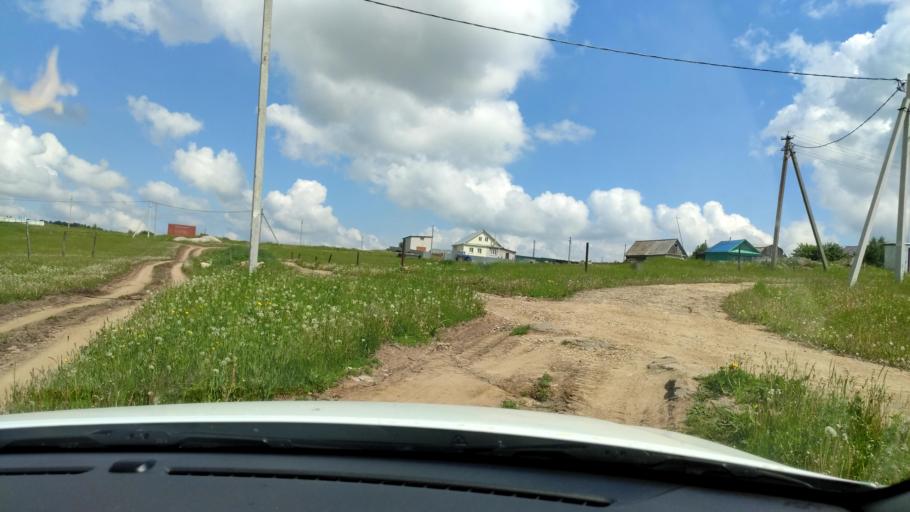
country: RU
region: Tatarstan
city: Vysokaya Gora
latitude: 56.0030
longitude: 49.3004
